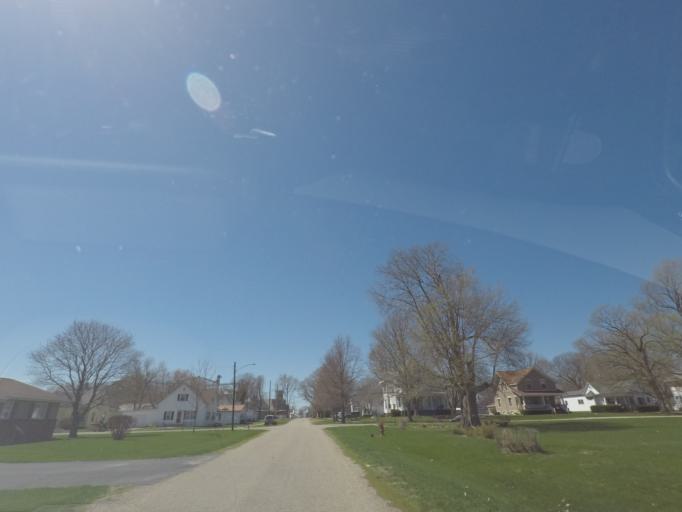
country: US
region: Illinois
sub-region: Macon County
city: Warrensburg
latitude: 39.9665
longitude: -89.1582
